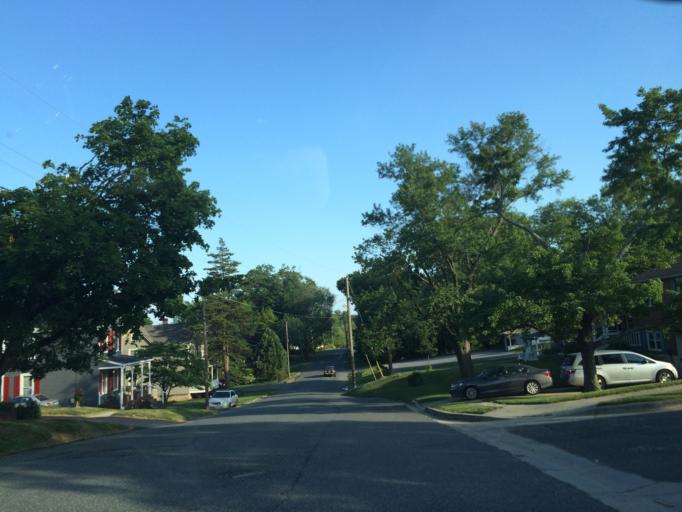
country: US
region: Maryland
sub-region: Baltimore County
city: Catonsville
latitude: 39.2762
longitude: -76.7286
